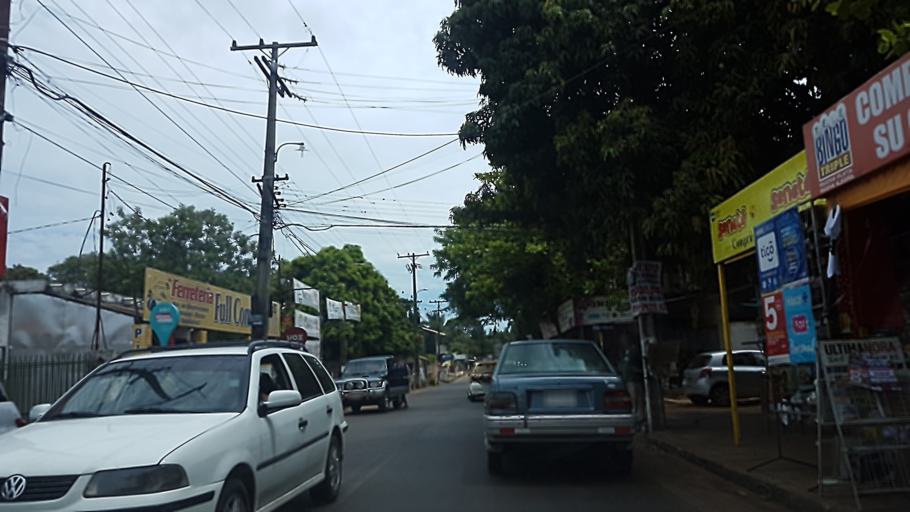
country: PY
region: Central
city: Capiata
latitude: -25.3473
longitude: -57.4616
